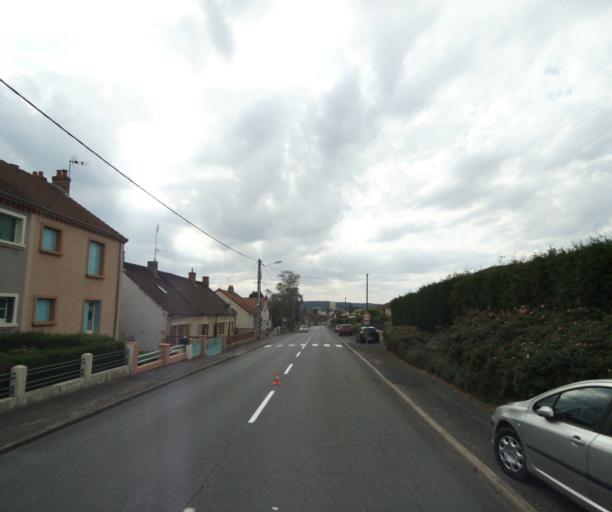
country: FR
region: Bourgogne
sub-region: Departement de Saone-et-Loire
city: Gueugnon
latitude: 46.6019
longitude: 4.0790
